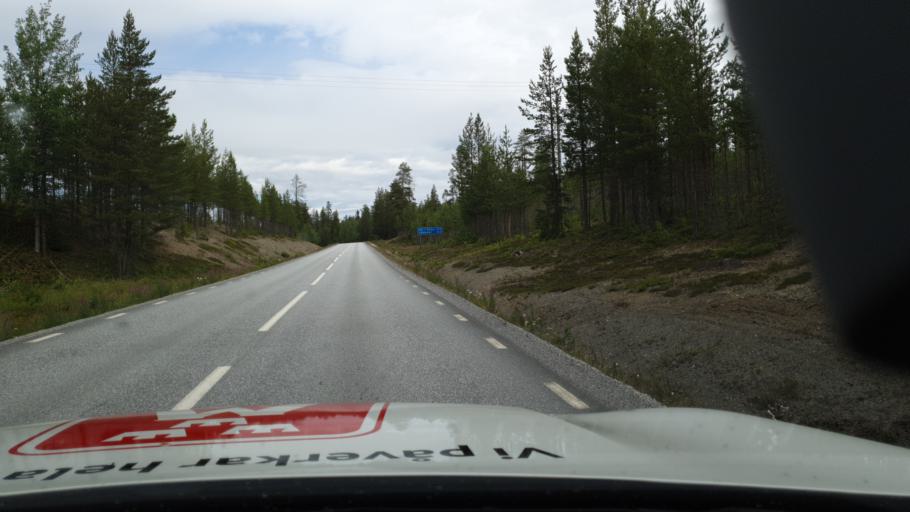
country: SE
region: Vaesterbotten
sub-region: Storumans Kommun
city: Fristad
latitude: 65.2609
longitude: 16.8325
